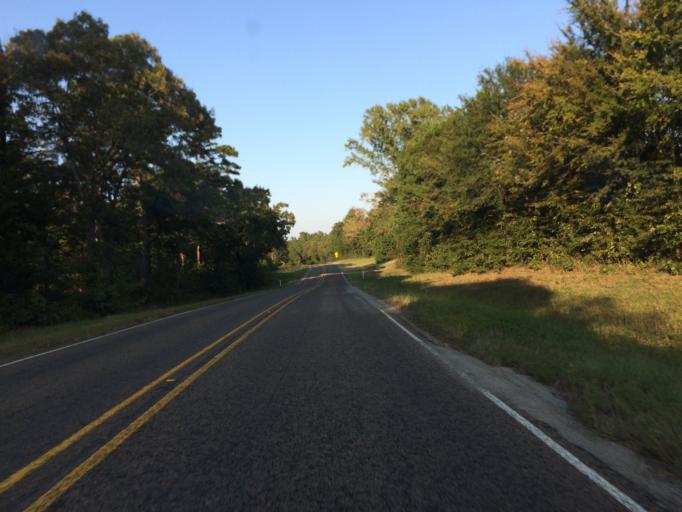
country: US
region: Texas
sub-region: Wood County
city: Mineola
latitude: 32.6911
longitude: -95.4144
